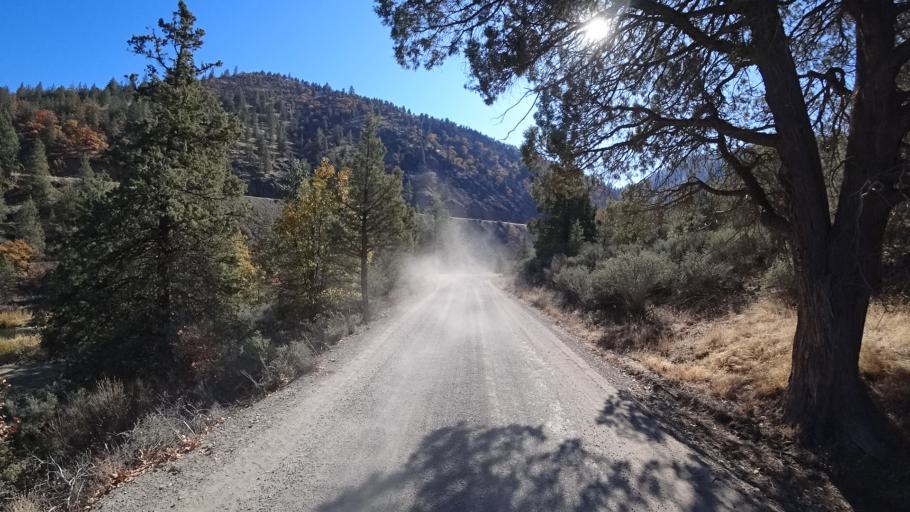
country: US
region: California
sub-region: Siskiyou County
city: Yreka
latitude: 41.7978
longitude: -122.6053
